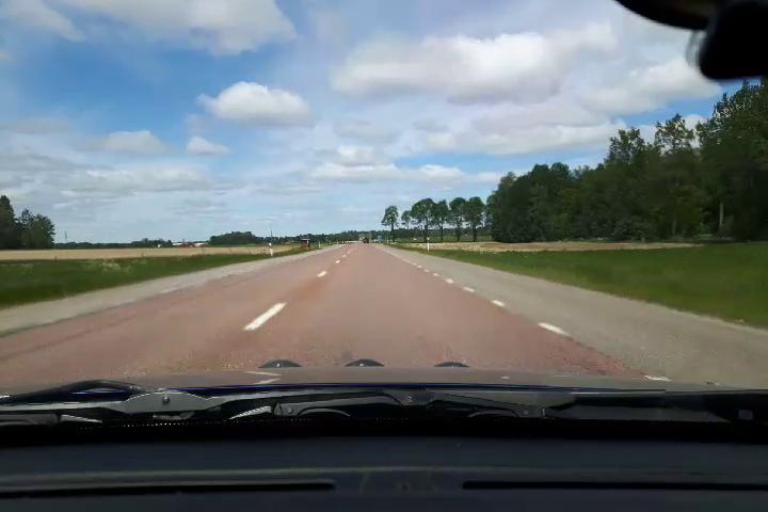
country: SE
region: Uppsala
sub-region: Osthammars Kommun
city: Bjorklinge
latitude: 60.0112
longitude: 17.5598
